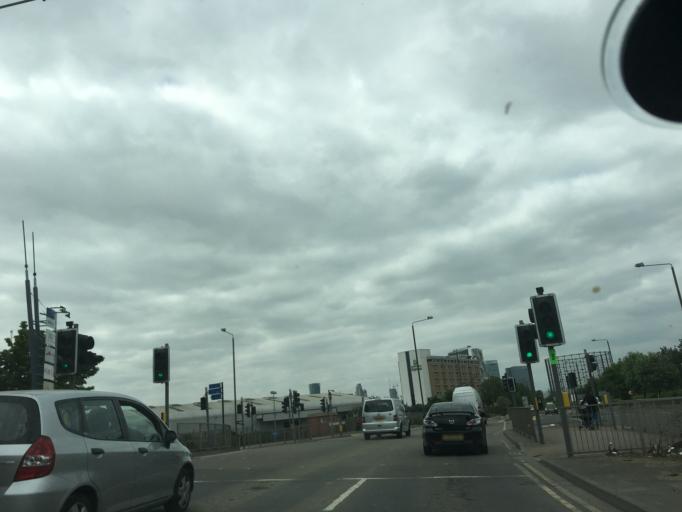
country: GB
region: England
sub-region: Greater London
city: Blackheath
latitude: 51.4910
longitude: 0.0133
